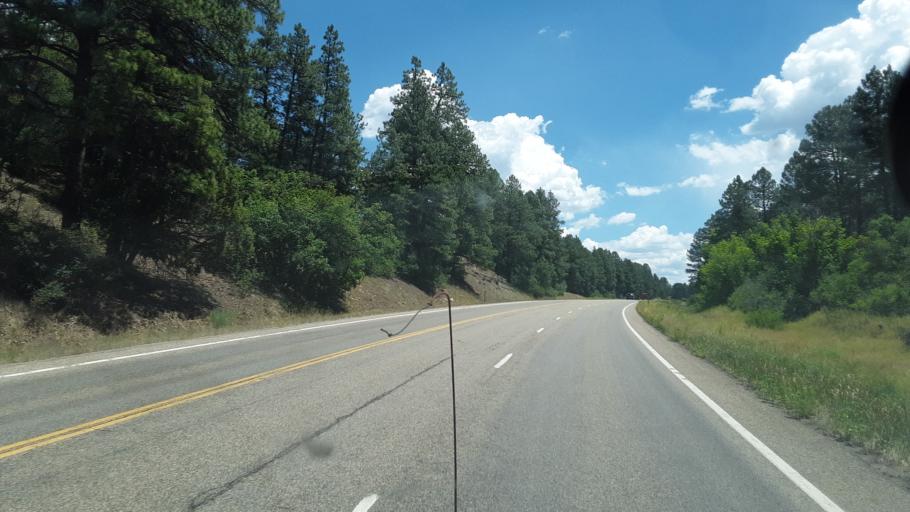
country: US
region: Colorado
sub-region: Archuleta County
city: Pagosa Springs
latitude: 37.2132
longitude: -107.2927
